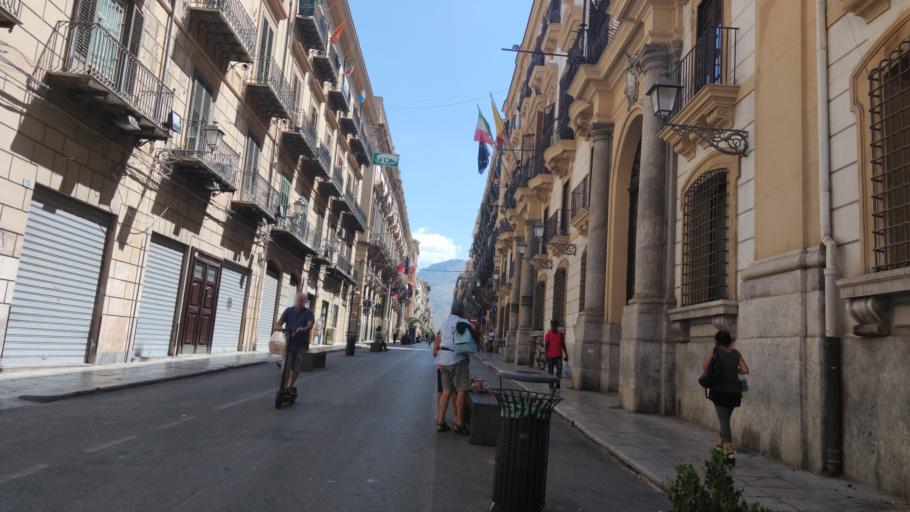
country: IT
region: Sicily
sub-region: Palermo
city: Palermo
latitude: 38.1129
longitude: 13.3633
